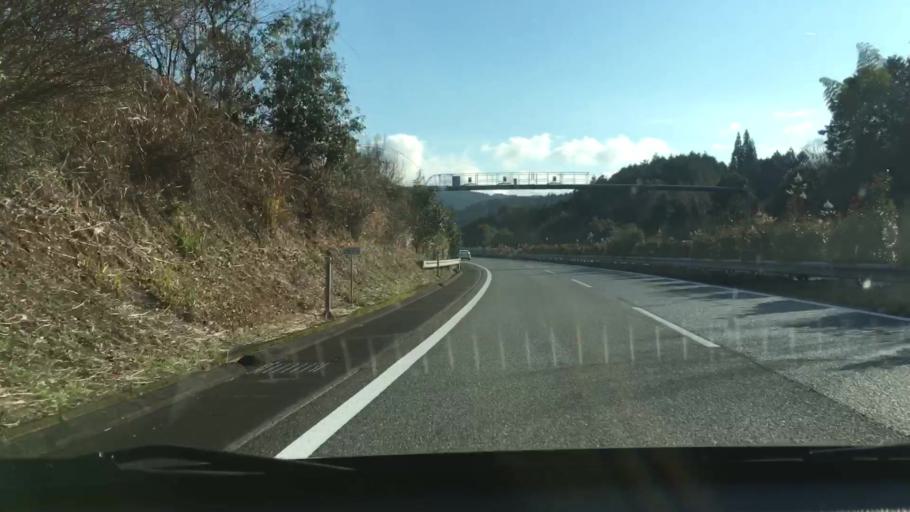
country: JP
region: Kumamoto
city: Hitoyoshi
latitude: 32.1885
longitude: 130.7768
